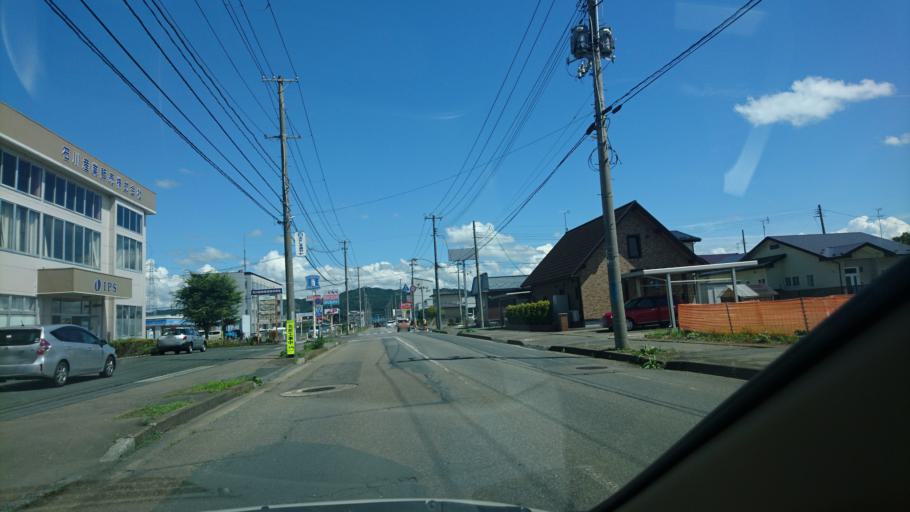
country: JP
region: Iwate
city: Kitakami
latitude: 39.2841
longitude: 141.1061
